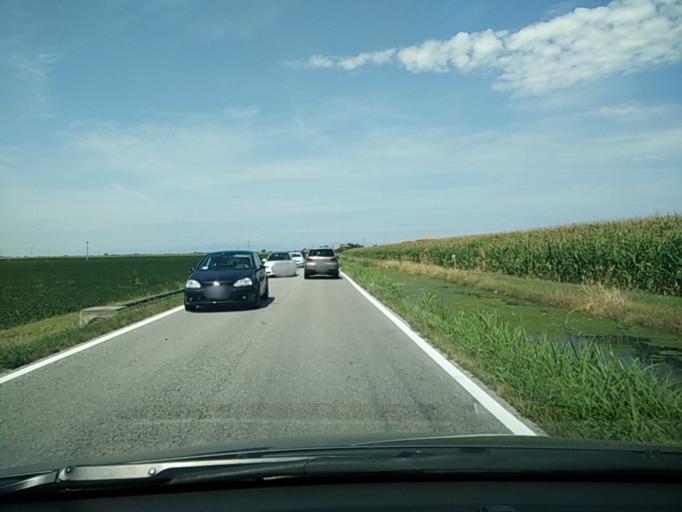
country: IT
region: Veneto
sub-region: Provincia di Venezia
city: Iesolo
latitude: 45.5640
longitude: 12.6343
